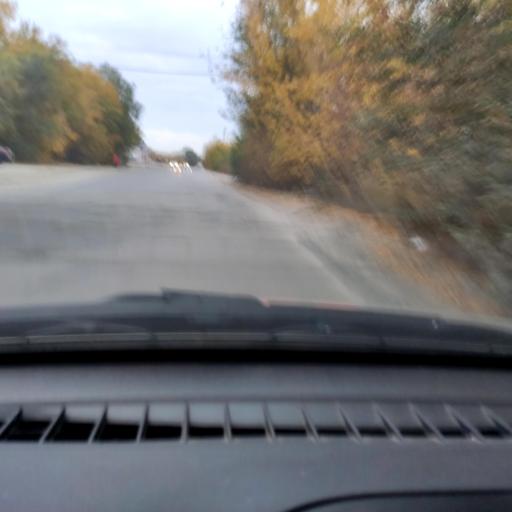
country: RU
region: Samara
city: Tol'yatti
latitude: 53.5744
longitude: 49.2882
